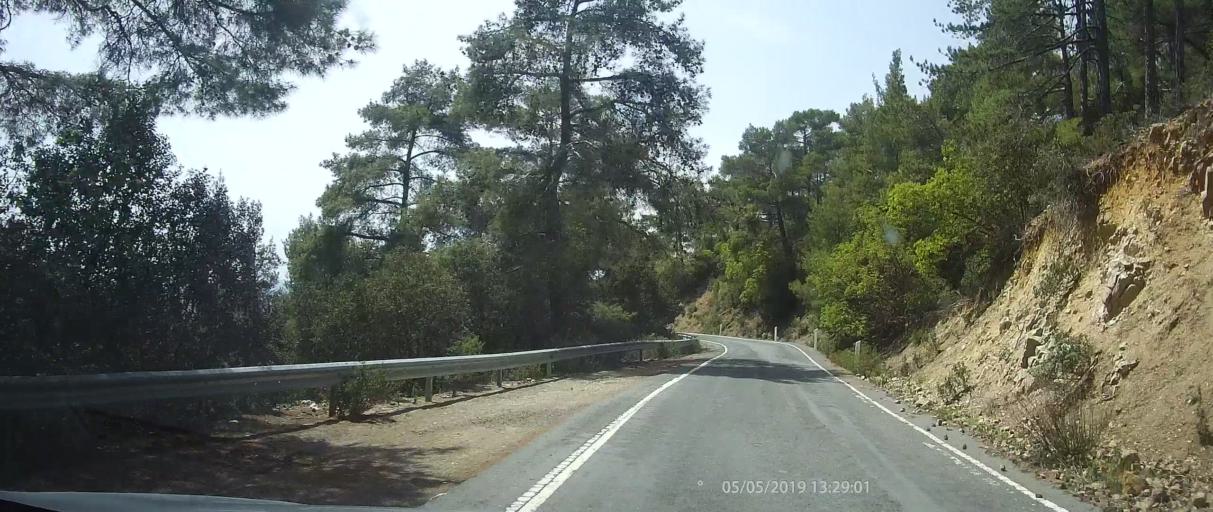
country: CY
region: Lefkosia
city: Kakopetria
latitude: 34.8973
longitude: 32.8514
